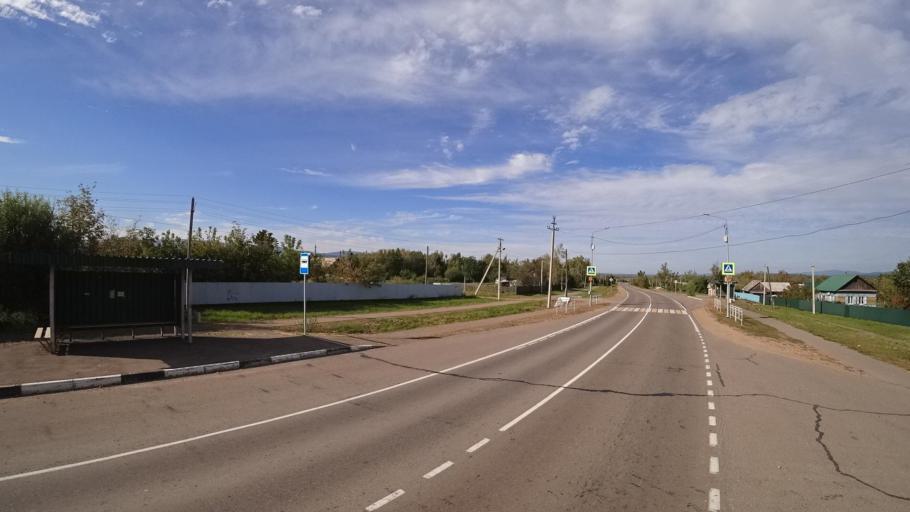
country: RU
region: Primorskiy
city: Dostoyevka
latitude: 44.3010
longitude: 133.4488
